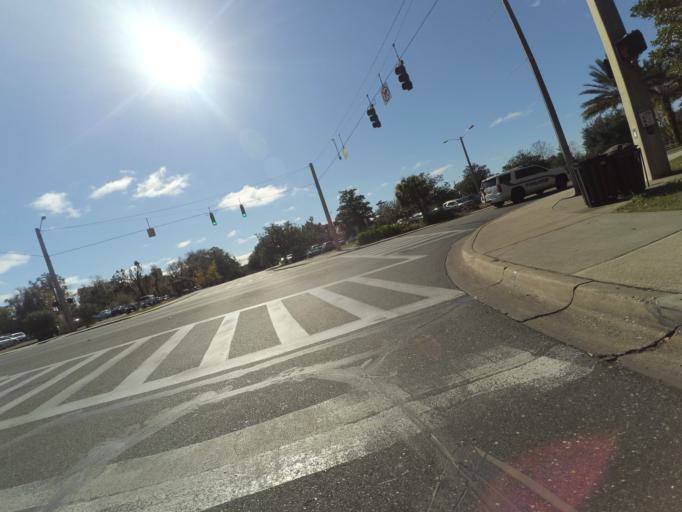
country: US
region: Florida
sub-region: Alachua County
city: Gainesville
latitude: 29.6452
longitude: -82.3469
